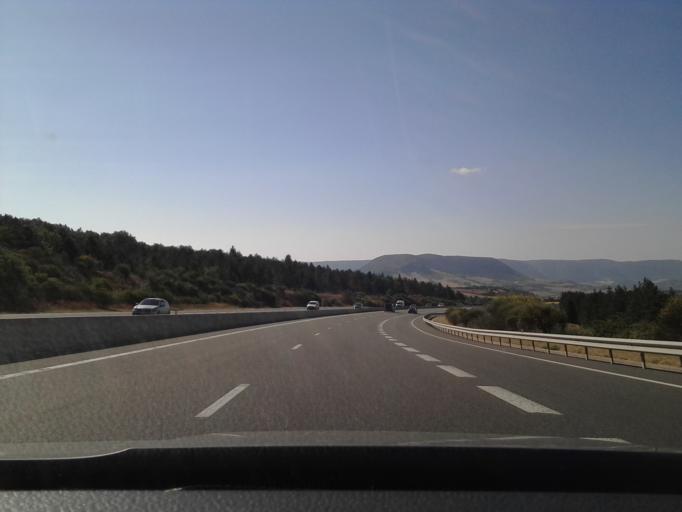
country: FR
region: Midi-Pyrenees
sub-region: Departement de l'Aveyron
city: Severac-le-Chateau
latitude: 44.2281
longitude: 3.0677
